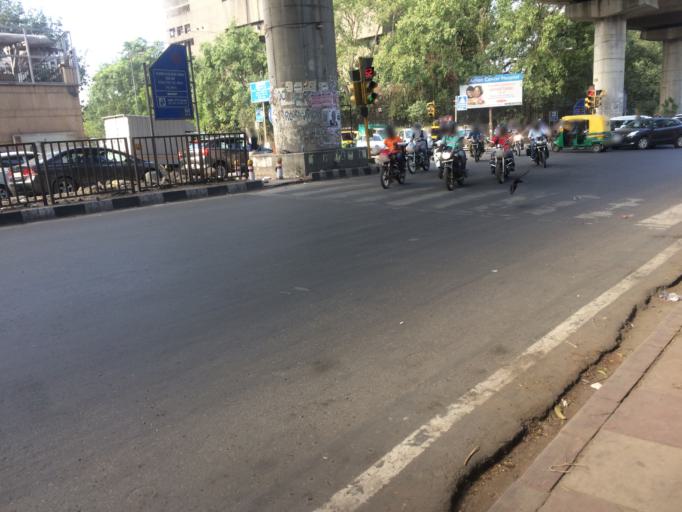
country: IN
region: NCT
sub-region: Central Delhi
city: Karol Bagh
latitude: 28.6429
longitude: 77.1806
